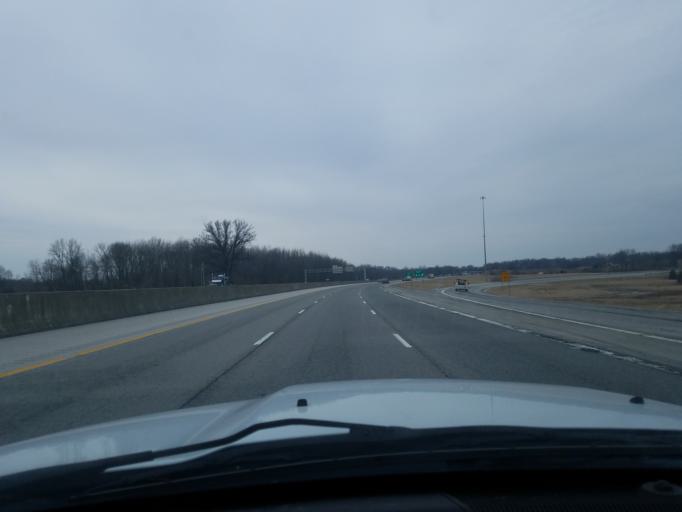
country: US
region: Kentucky
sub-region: Barren County
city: Cave City
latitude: 37.0576
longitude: -86.1140
